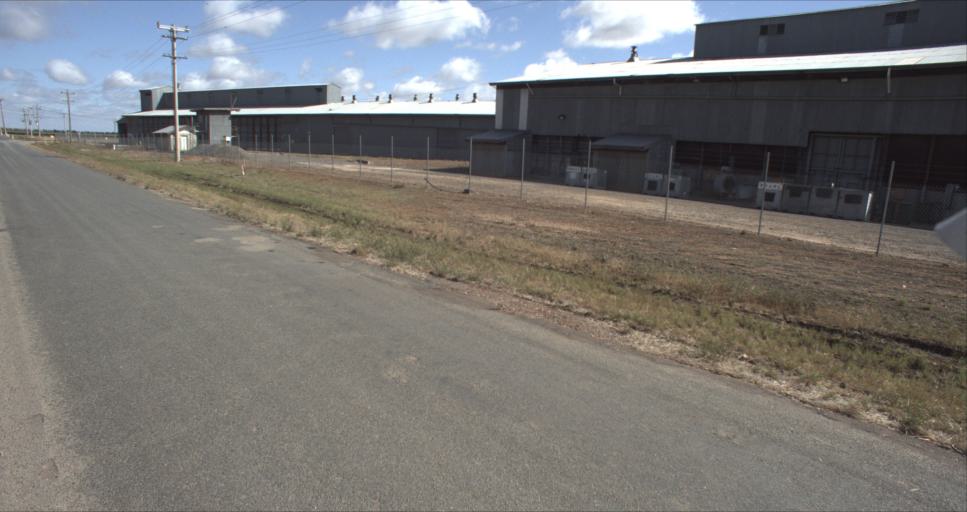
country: AU
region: New South Wales
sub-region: Murrumbidgee Shire
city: Darlington Point
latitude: -34.5147
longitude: 146.1803
